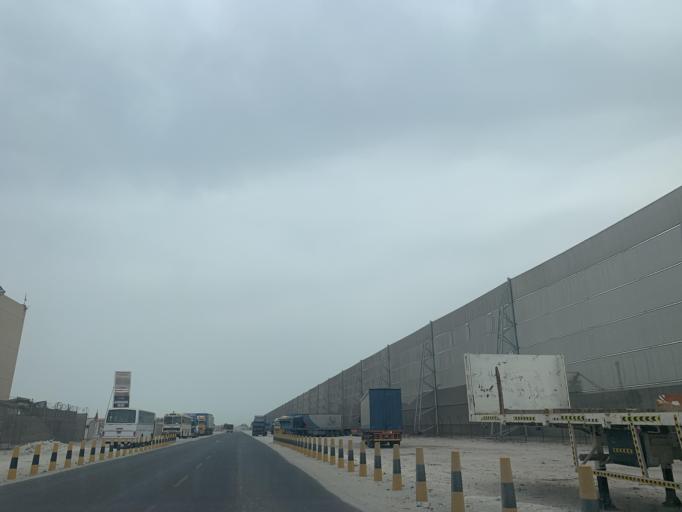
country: BH
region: Muharraq
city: Al Hadd
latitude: 26.2080
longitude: 50.6795
